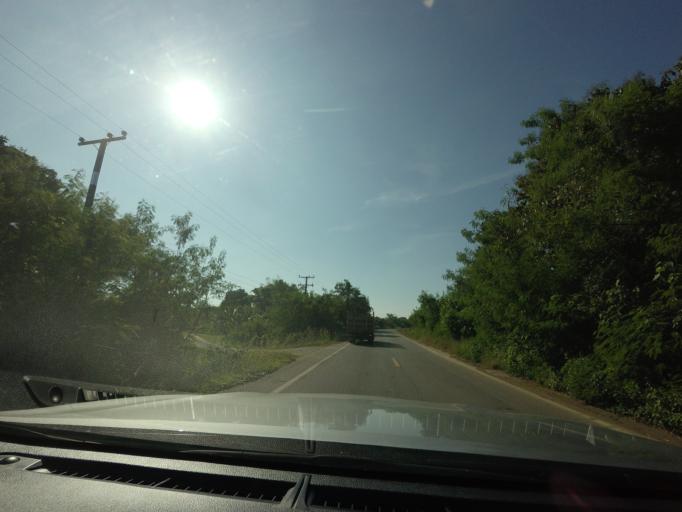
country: TH
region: Phrae
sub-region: Amphoe Wang Chin
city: Wang Chin
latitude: 17.7056
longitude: 99.6852
